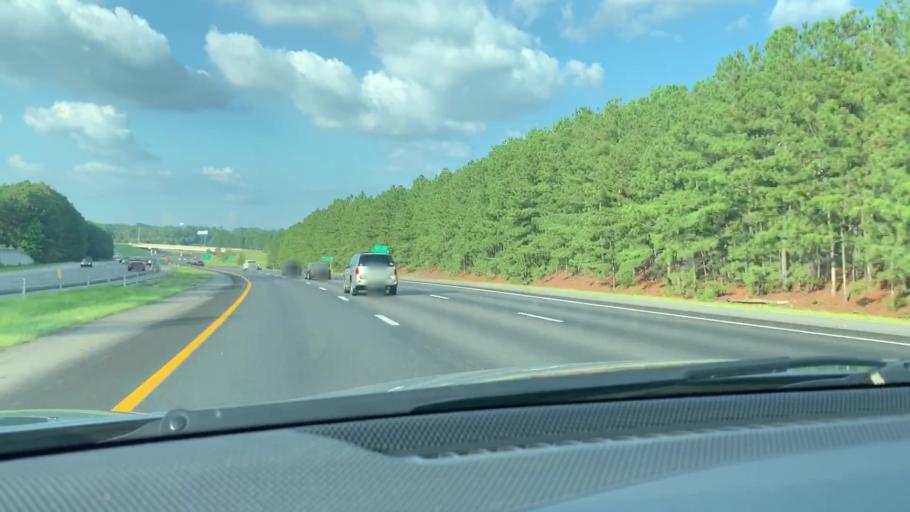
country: US
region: South Carolina
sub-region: Richland County
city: Woodfield
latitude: 34.0343
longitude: -80.9385
